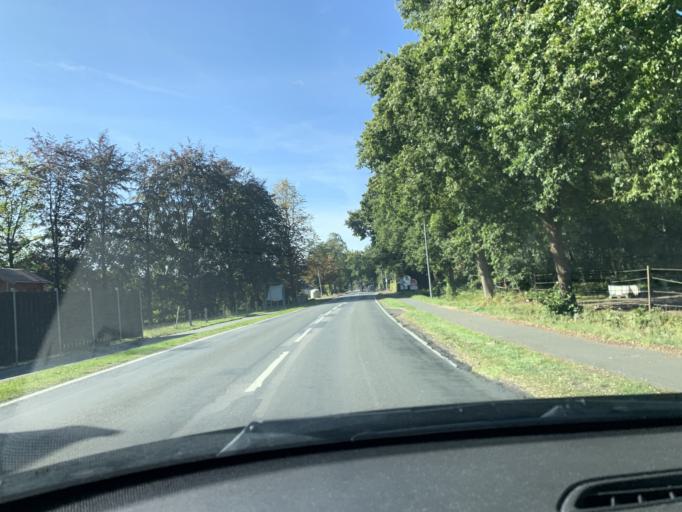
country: DE
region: Lower Saxony
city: Barssel
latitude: 53.1720
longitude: 7.7517
